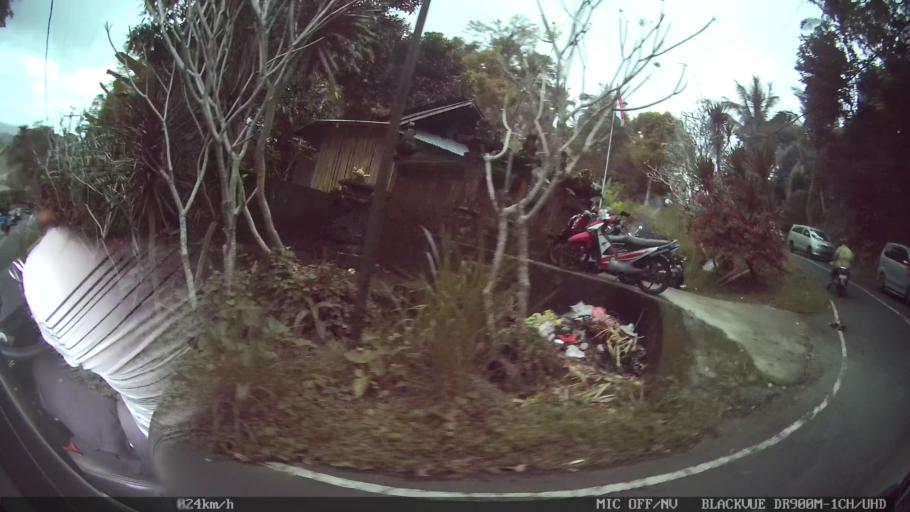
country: ID
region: Bali
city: Peneng
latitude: -8.3682
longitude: 115.2184
